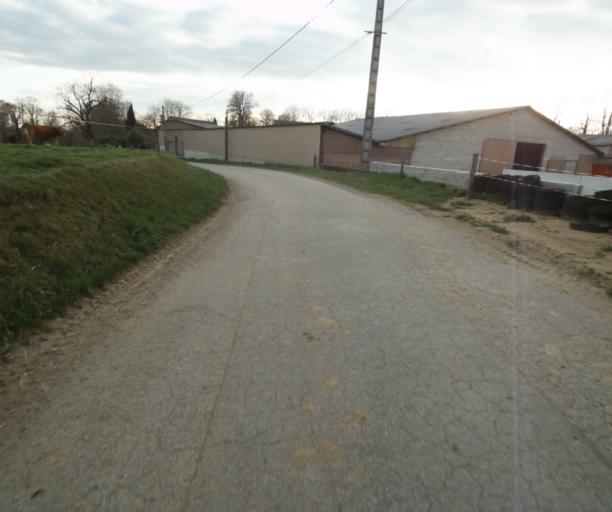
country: FR
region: Limousin
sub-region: Departement de la Correze
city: Saint-Clement
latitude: 45.3598
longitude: 1.6220
